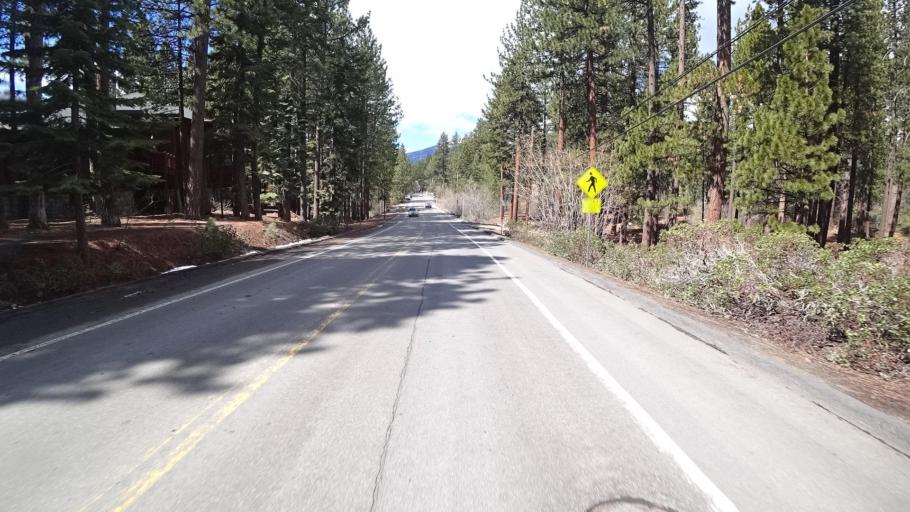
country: US
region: Nevada
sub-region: Washoe County
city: Incline Village
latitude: 39.2419
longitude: -119.9411
